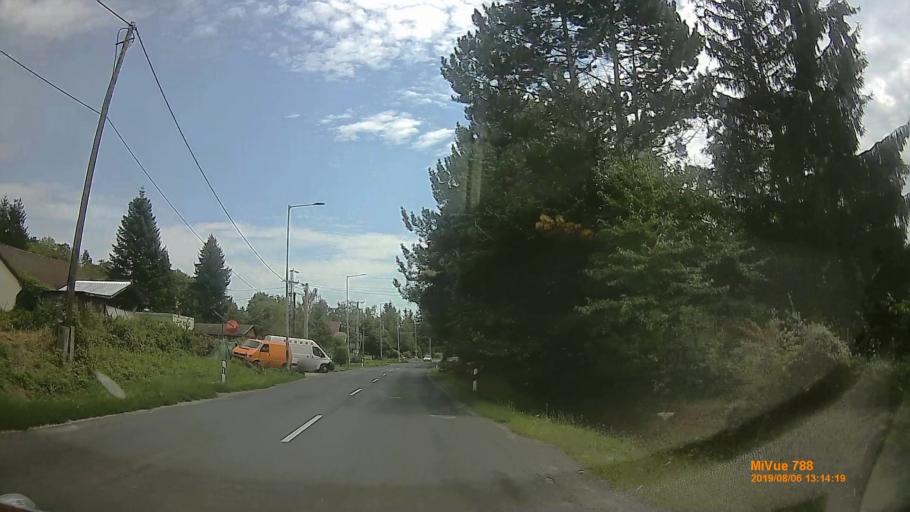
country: HU
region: Vas
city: Koszeg
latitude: 47.4051
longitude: 16.5320
